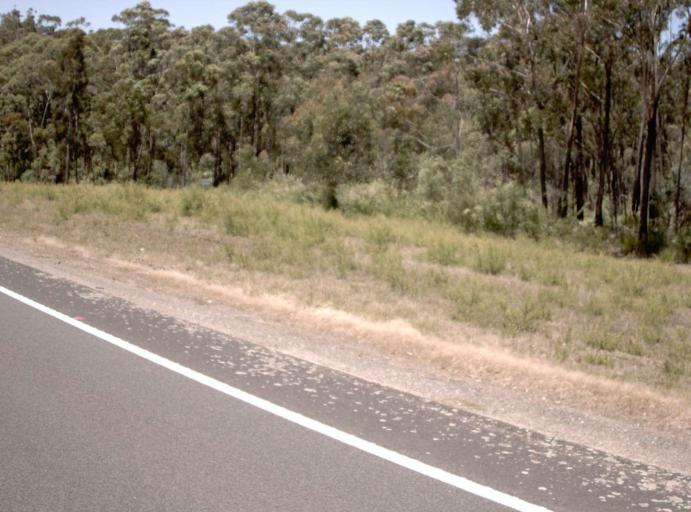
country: AU
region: Victoria
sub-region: East Gippsland
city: Lakes Entrance
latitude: -37.7487
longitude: 148.3714
